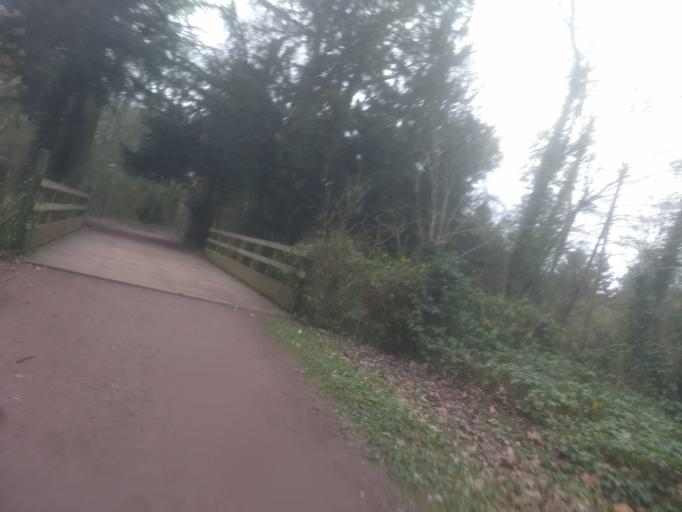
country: FR
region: Nord-Pas-de-Calais
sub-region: Departement du Pas-de-Calais
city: Saint-Laurent-Blangy
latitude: 50.3014
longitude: 2.8107
